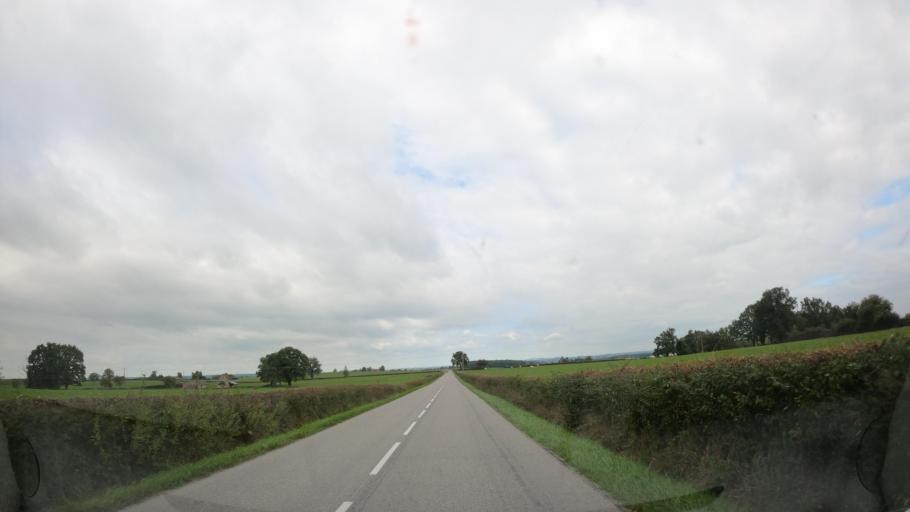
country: FR
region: Auvergne
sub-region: Departement de l'Allier
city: Saint-Gerand-le-Puy
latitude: 46.2902
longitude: 3.5604
